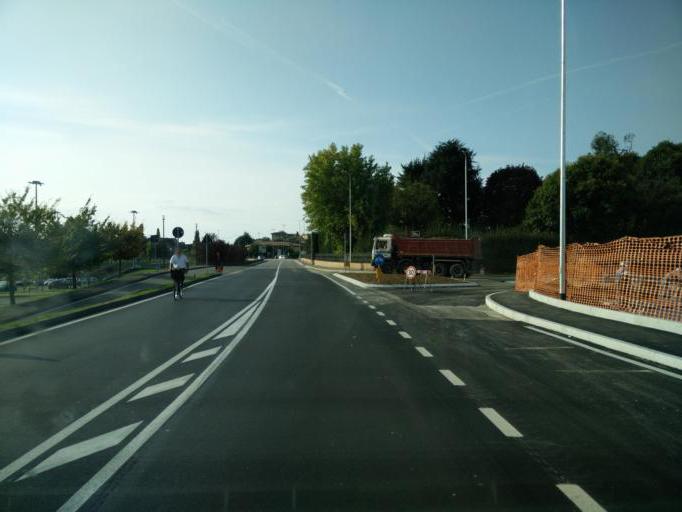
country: IT
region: Lombardy
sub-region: Provincia di Brescia
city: Colombaro-Timoline
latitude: 45.6432
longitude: 10.0117
